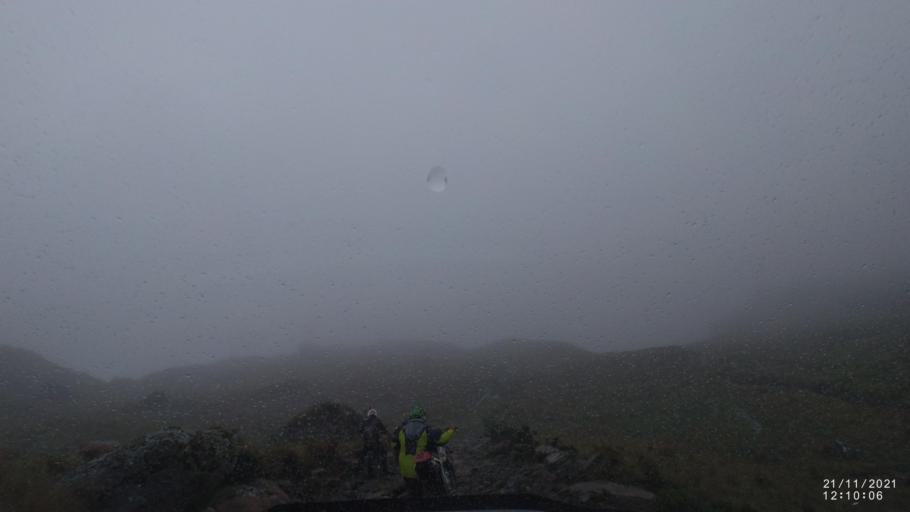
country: BO
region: Cochabamba
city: Cochabamba
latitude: -16.9443
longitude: -66.2573
